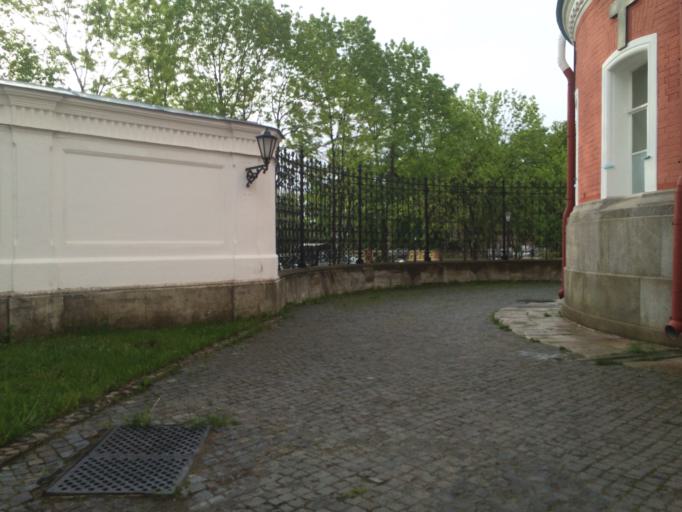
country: RU
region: Republic of Karelia
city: Lyaskelya
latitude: 61.3893
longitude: 30.9460
